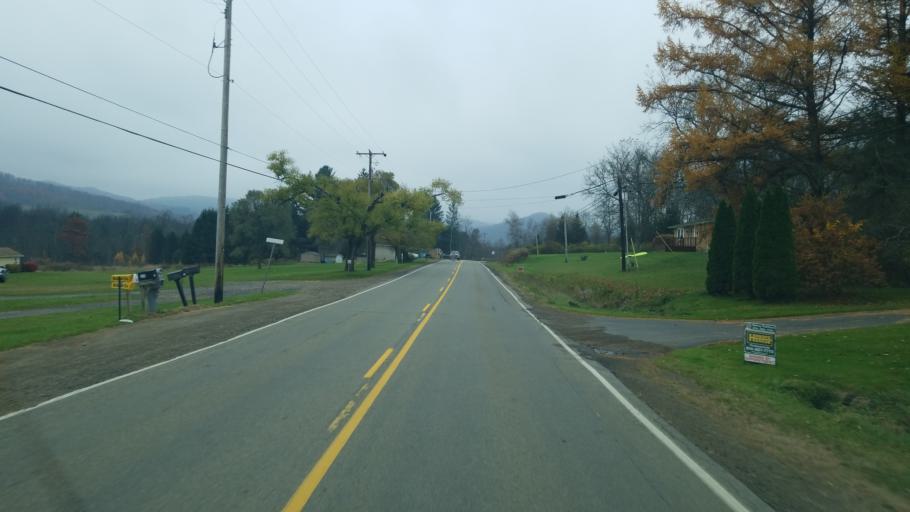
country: US
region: Pennsylvania
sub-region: McKean County
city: Smethport
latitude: 41.8389
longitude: -78.4337
